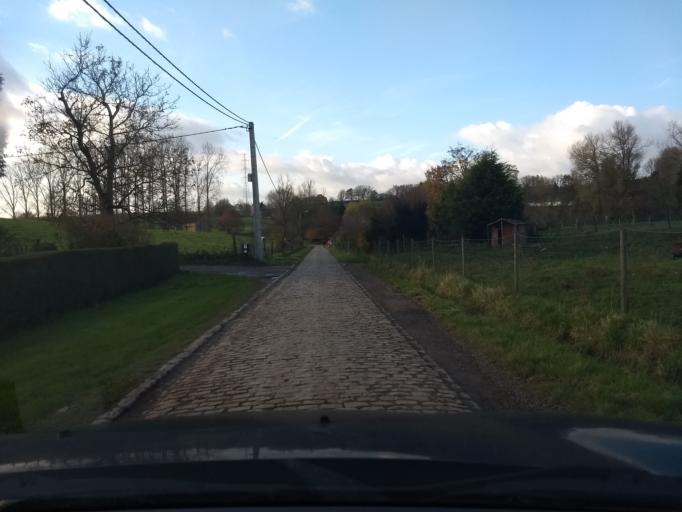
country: BE
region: Wallonia
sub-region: Province du Brabant Wallon
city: Ittre
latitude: 50.6033
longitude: 4.2600
